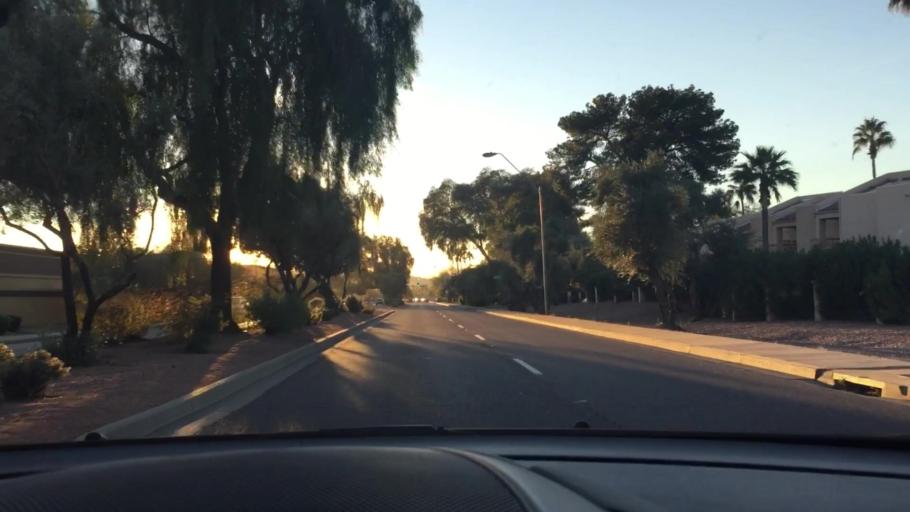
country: US
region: Arizona
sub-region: Maricopa County
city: Scottsdale
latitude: 33.5709
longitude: -111.8803
